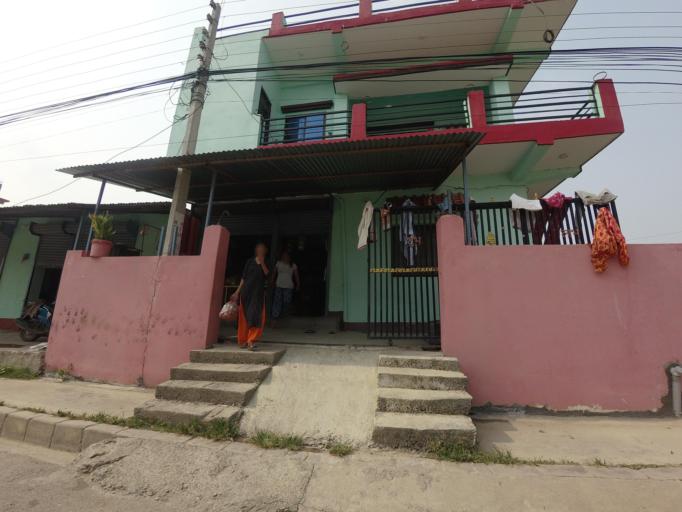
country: NP
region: Western Region
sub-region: Lumbini Zone
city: Bhairahawa
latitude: 27.5027
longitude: 83.4709
